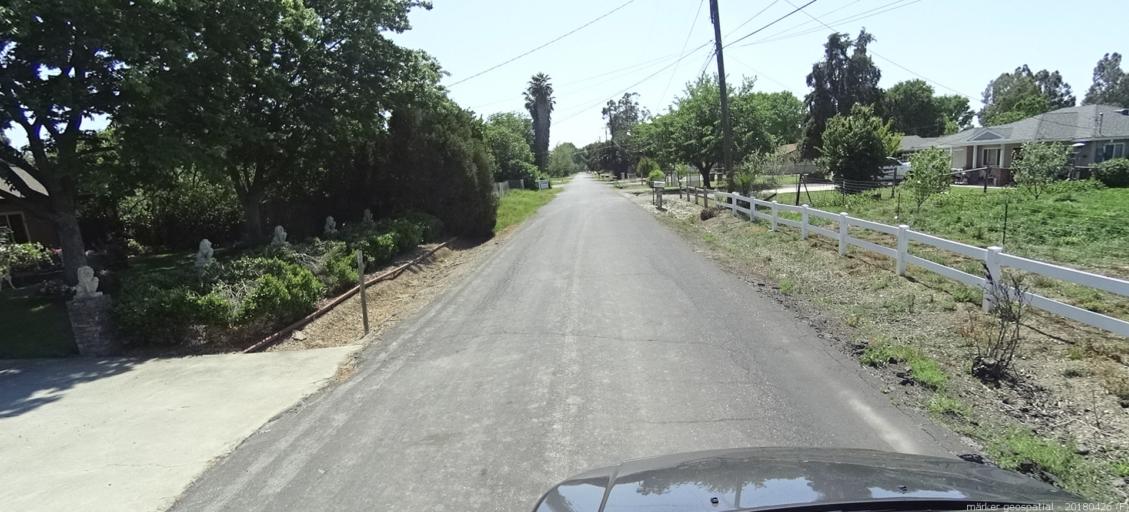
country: US
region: California
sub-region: Yolo County
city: West Sacramento
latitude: 38.5460
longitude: -121.5466
